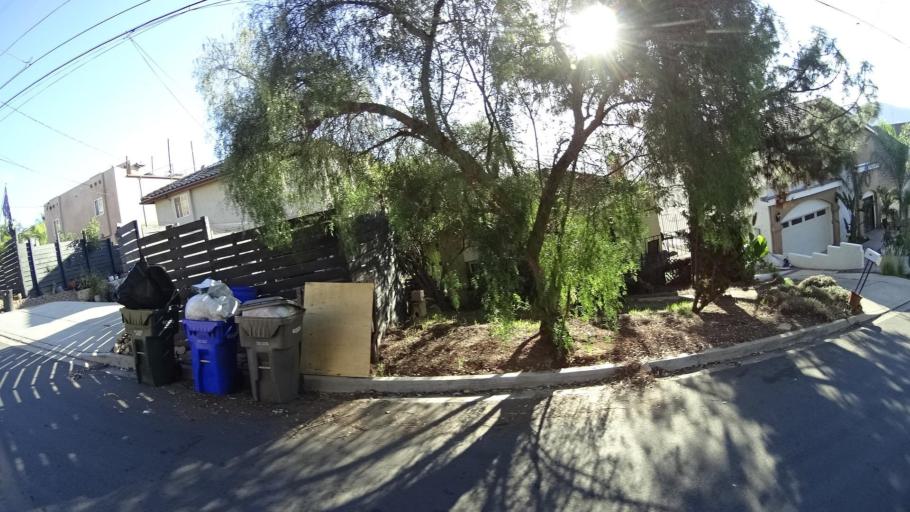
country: US
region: California
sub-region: San Diego County
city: La Presa
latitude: 32.7216
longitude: -116.9863
